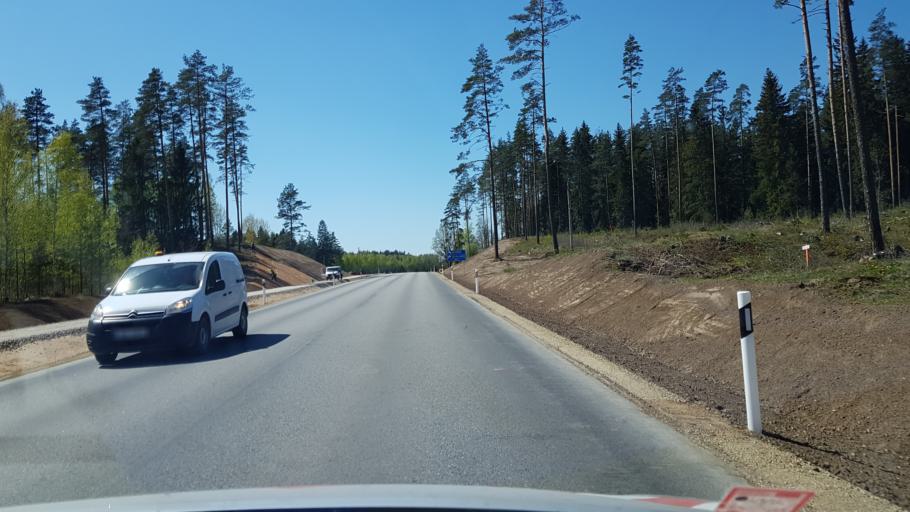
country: EE
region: Vorumaa
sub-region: Voru linn
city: Voru
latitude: 57.8740
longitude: 26.8155
